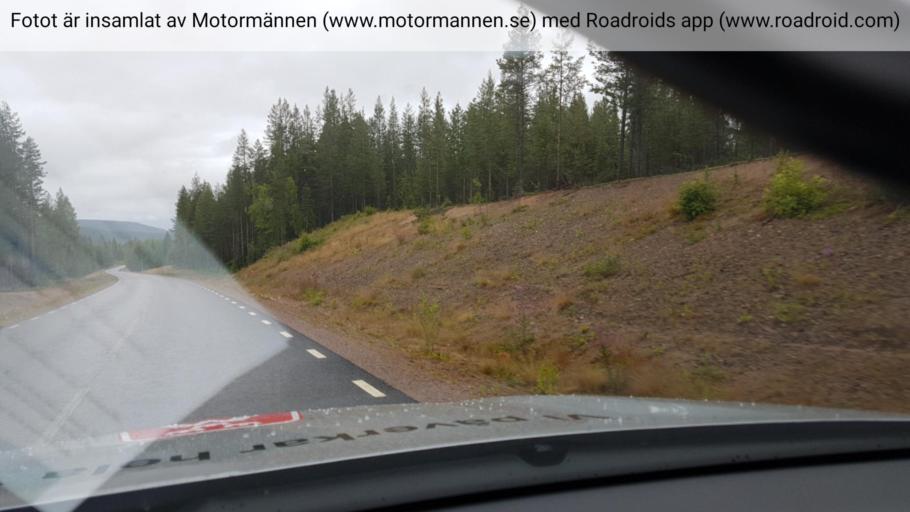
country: SE
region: Norrbotten
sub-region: Gallivare Kommun
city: Gaellivare
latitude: 66.6175
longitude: 20.4322
